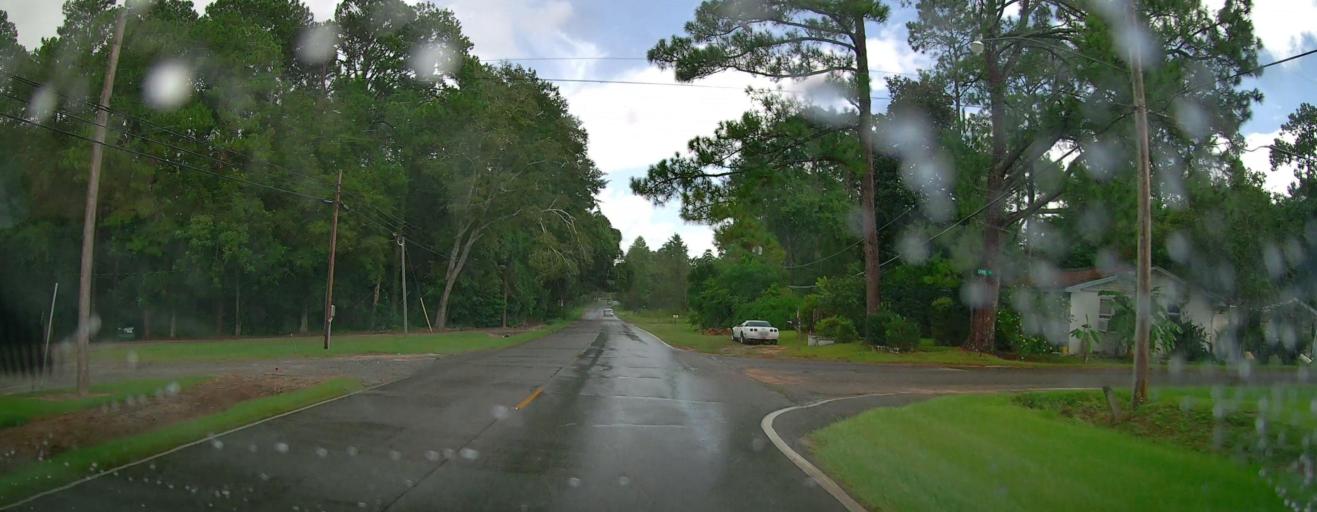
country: US
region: Georgia
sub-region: Ben Hill County
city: Fitzgerald
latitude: 31.7143
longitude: -83.2739
